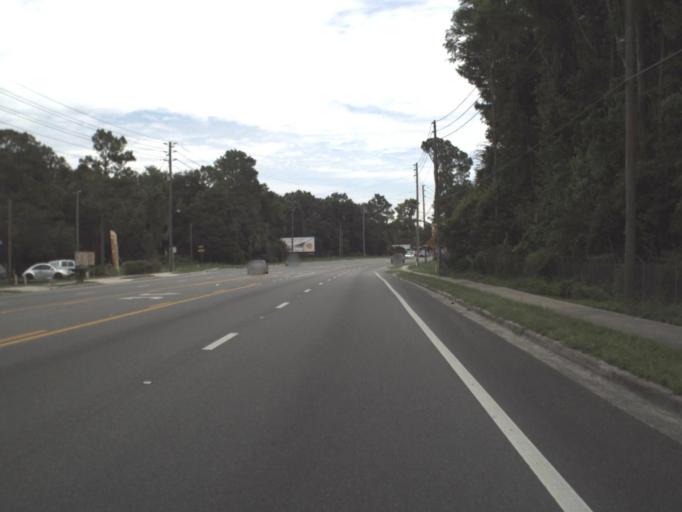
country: US
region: Florida
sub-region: Citrus County
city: Crystal River
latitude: 28.8944
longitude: -82.5541
